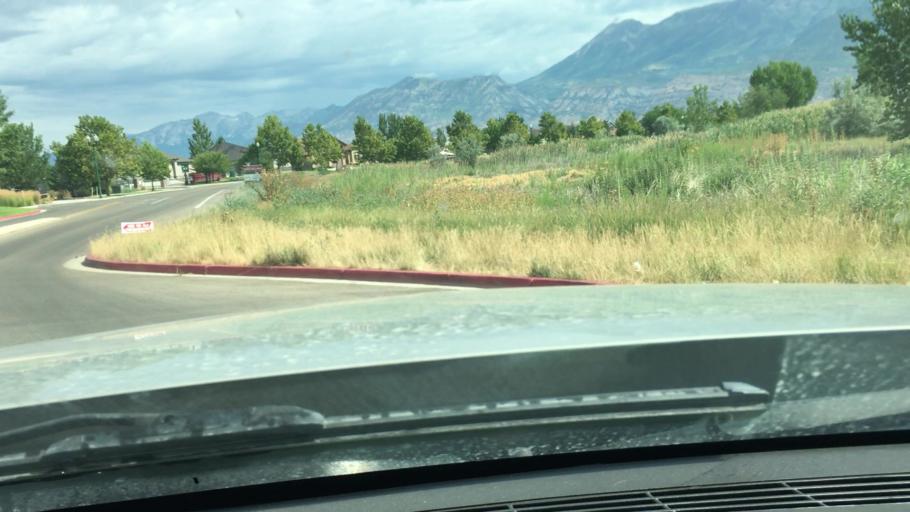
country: US
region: Utah
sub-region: Utah County
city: Orem
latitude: 40.2831
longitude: -111.7427
